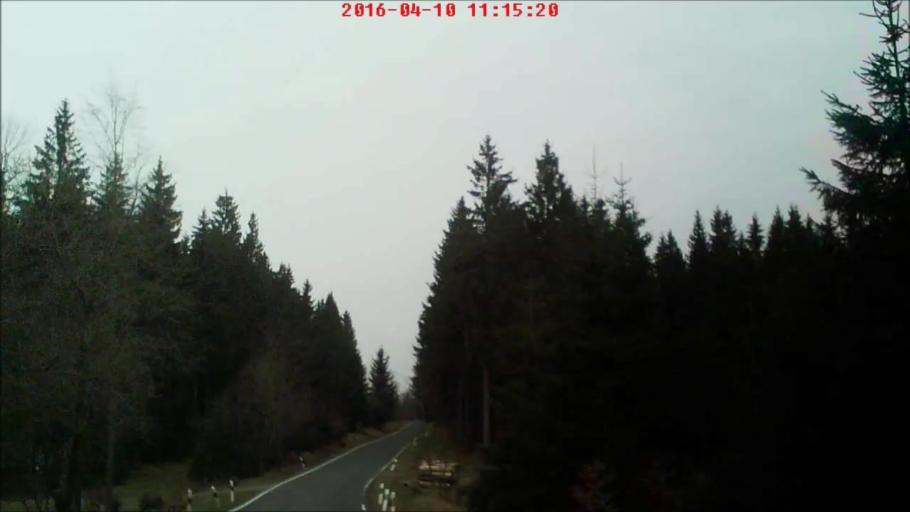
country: DE
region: Thuringia
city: Frauenwald
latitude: 50.5974
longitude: 10.8484
